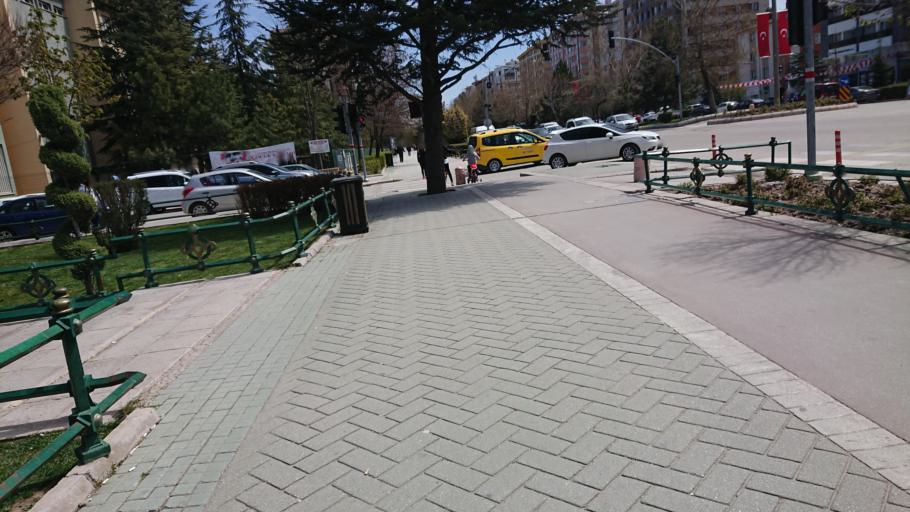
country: TR
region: Eskisehir
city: Eskisehir
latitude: 39.7653
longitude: 30.5135
